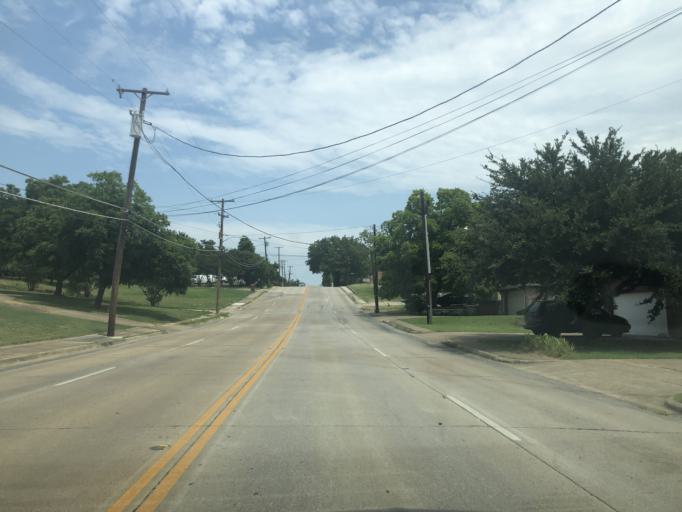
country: US
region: Texas
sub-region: Dallas County
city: Grand Prairie
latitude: 32.7488
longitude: -97.0155
